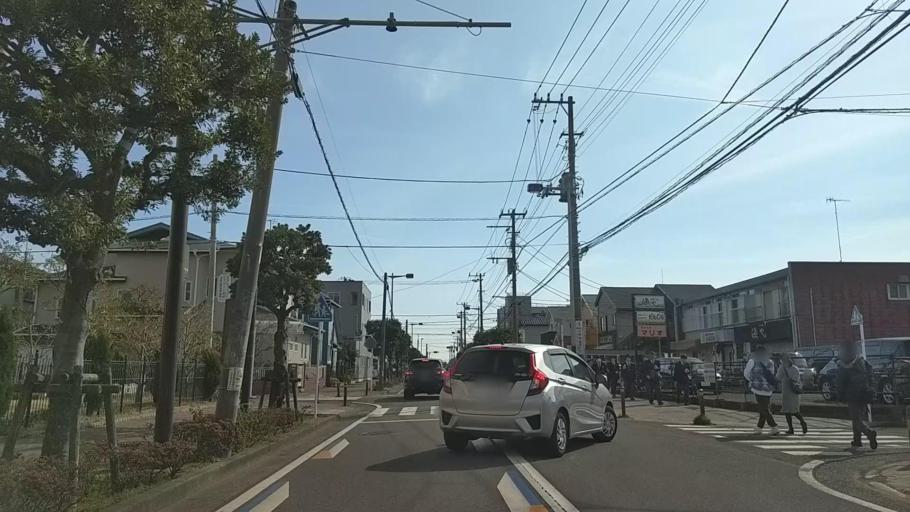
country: JP
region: Kanagawa
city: Fujisawa
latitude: 35.3277
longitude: 139.4477
